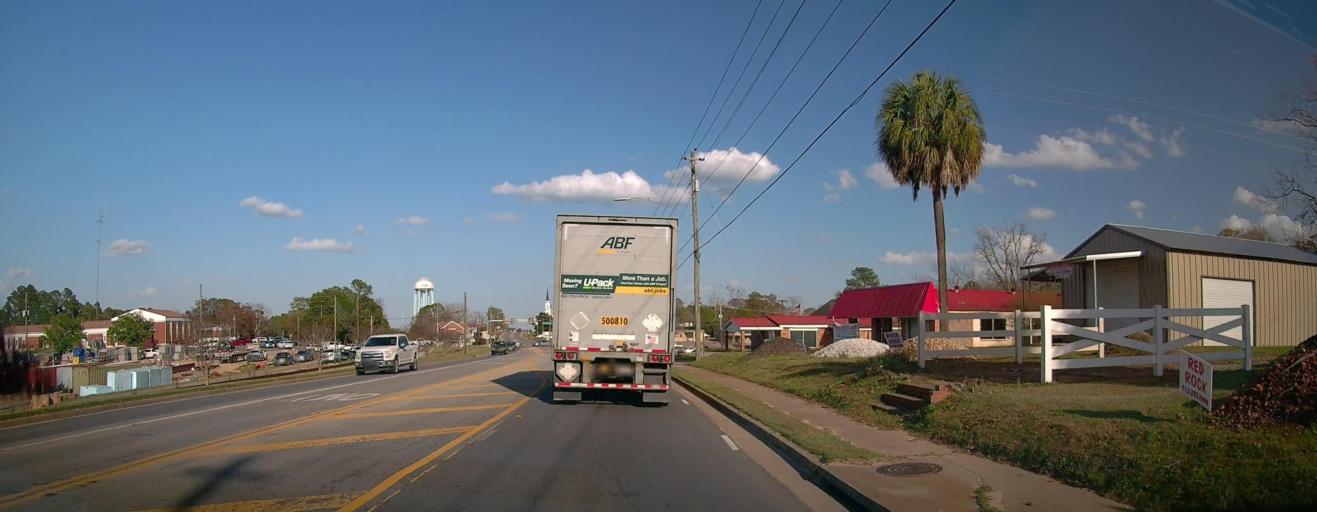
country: US
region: Georgia
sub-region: Toombs County
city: Lyons
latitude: 32.2017
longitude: -82.3296
